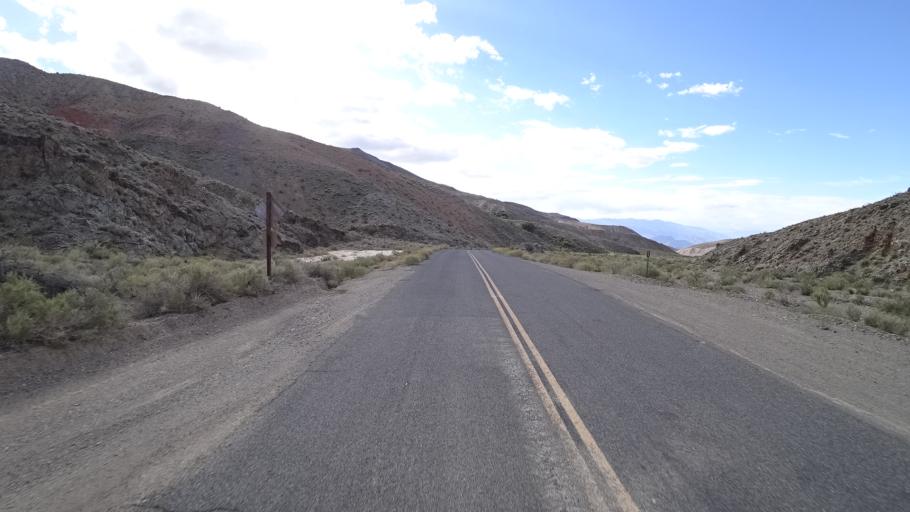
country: US
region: Nevada
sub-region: Nye County
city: Beatty
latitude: 36.4329
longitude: -117.1931
